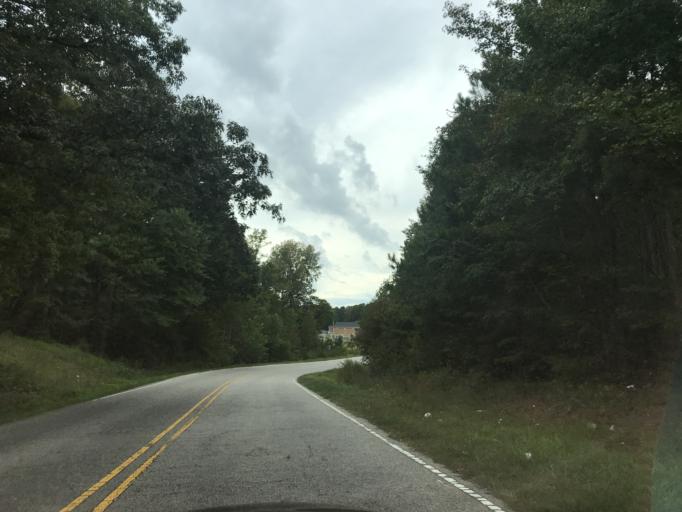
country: US
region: North Carolina
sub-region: Wake County
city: Rolesville
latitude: 35.9782
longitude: -78.3755
